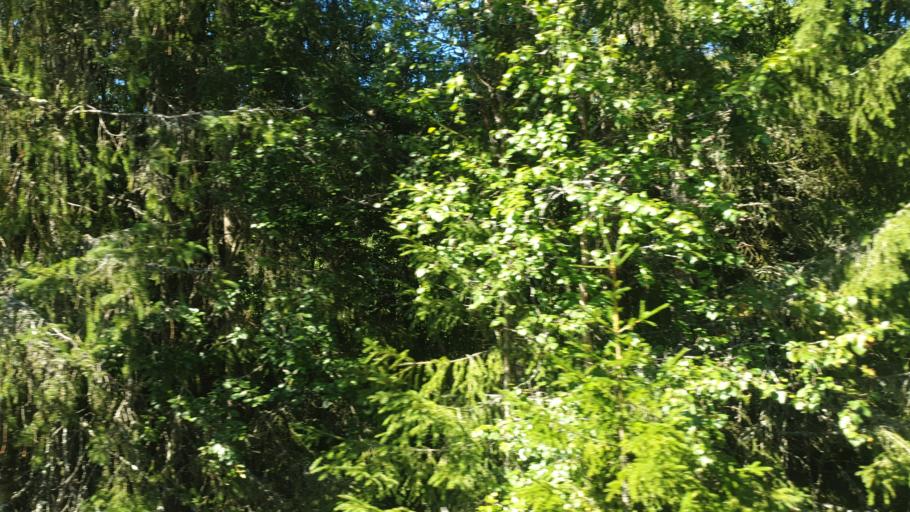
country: NO
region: Sor-Trondelag
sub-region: Meldal
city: Meldal
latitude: 63.1482
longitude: 9.7173
